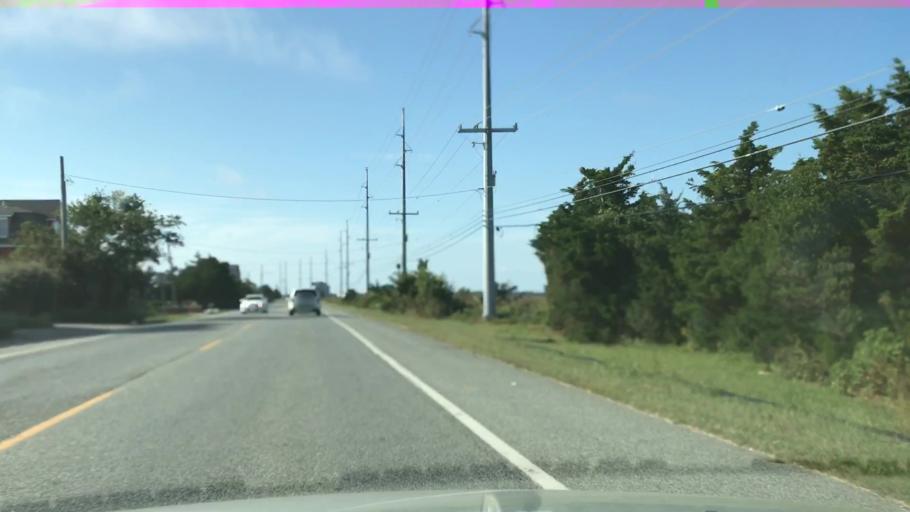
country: US
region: New Jersey
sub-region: Cape May County
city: Cape May Court House
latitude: 39.0644
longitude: -74.7780
